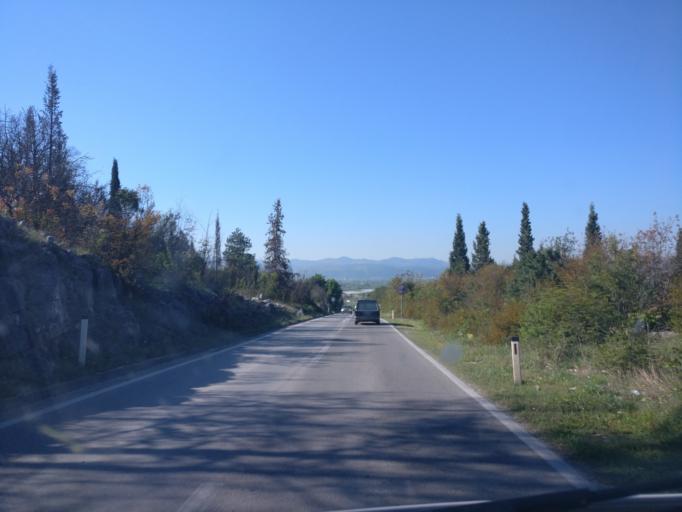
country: BA
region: Federation of Bosnia and Herzegovina
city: Tasovcici
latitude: 43.1153
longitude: 17.7219
